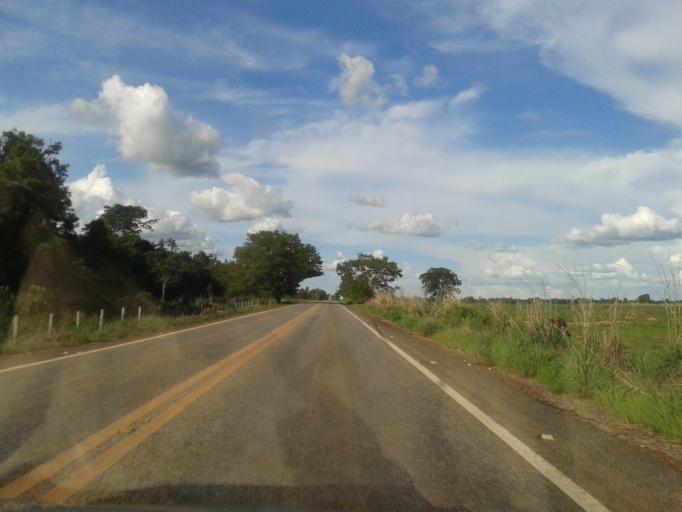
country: BR
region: Goias
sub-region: Mozarlandia
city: Mozarlandia
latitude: -14.5543
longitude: -50.4948
